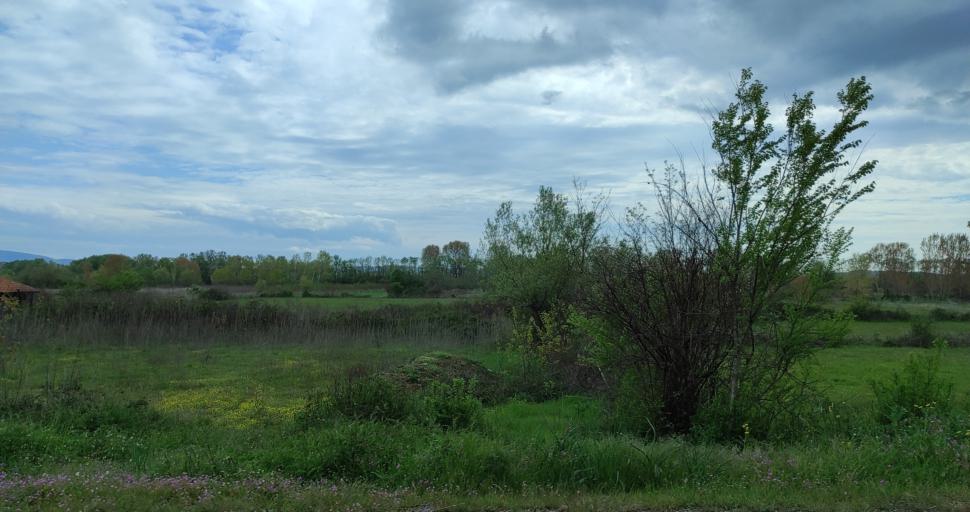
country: AL
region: Shkoder
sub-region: Rrethi i Shkodres
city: Dajc
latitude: 42.0110
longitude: 19.4145
